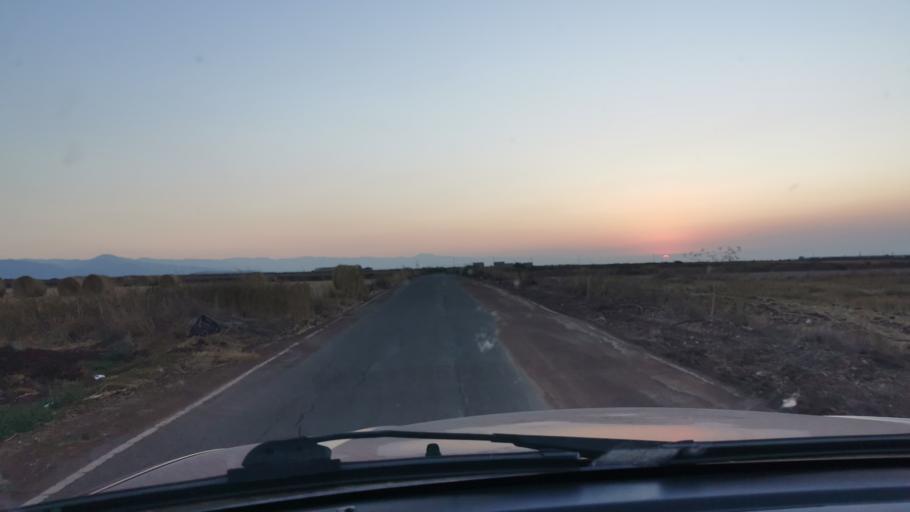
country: CY
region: Lefkosia
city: Peristerona
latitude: 35.0983
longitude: 33.0826
